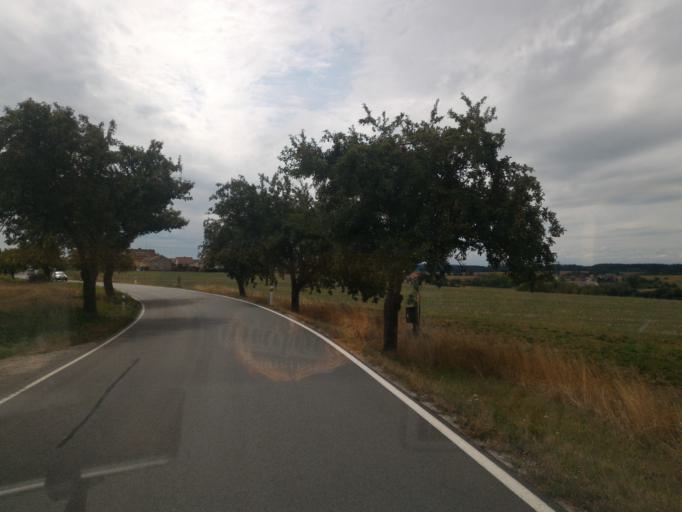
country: CZ
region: Jihocesky
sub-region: Okres Jindrichuv Hradec
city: Dacice
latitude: 49.0903
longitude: 15.4259
